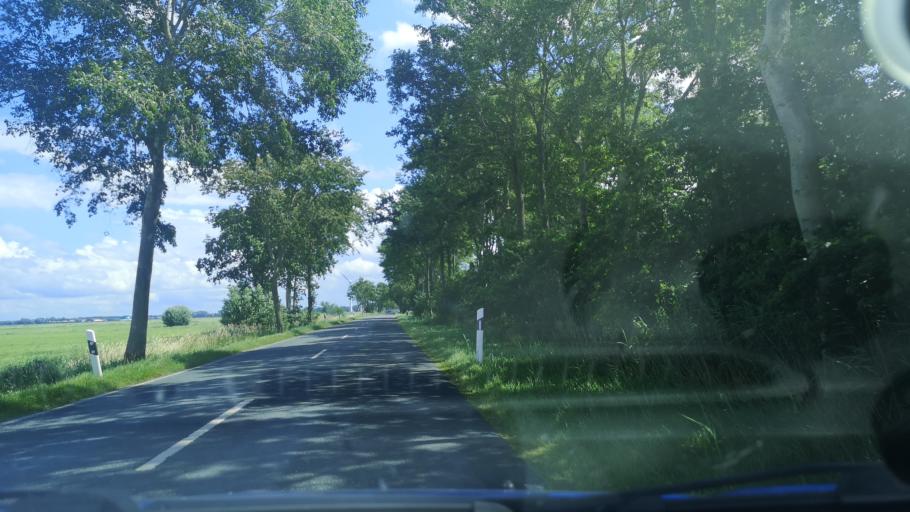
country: DE
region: Lower Saxony
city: Mulsum
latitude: 53.6463
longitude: 8.5428
